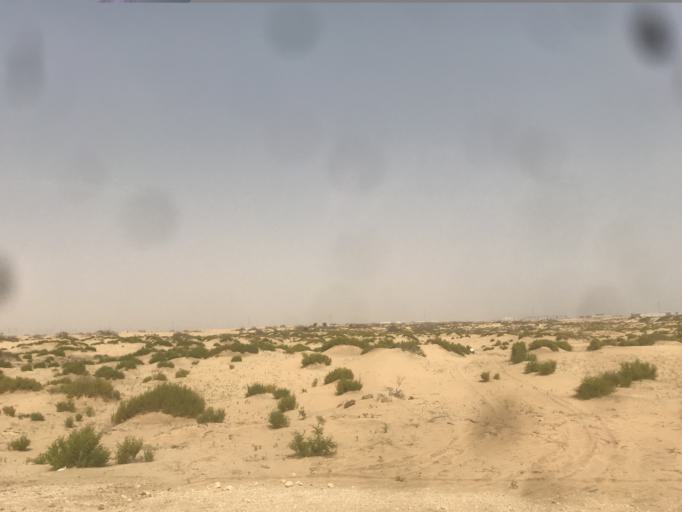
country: SA
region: Eastern Province
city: Abqaiq
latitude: 25.9094
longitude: 49.9360
